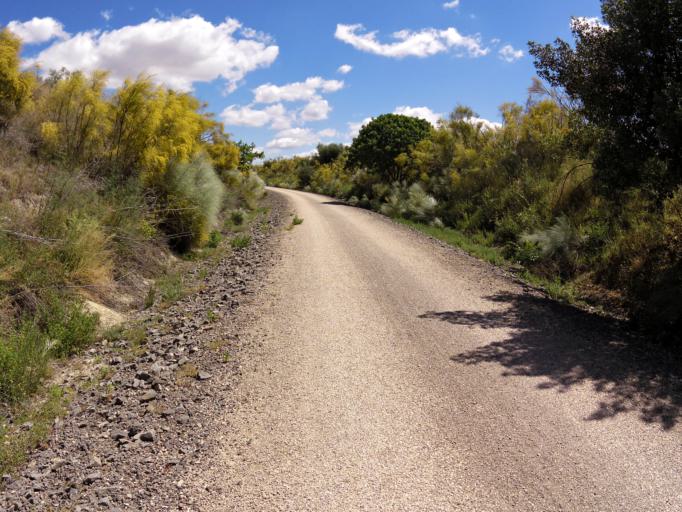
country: ES
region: Andalusia
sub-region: Provincia de Jaen
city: Alcaudete
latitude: 37.6494
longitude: -4.0638
